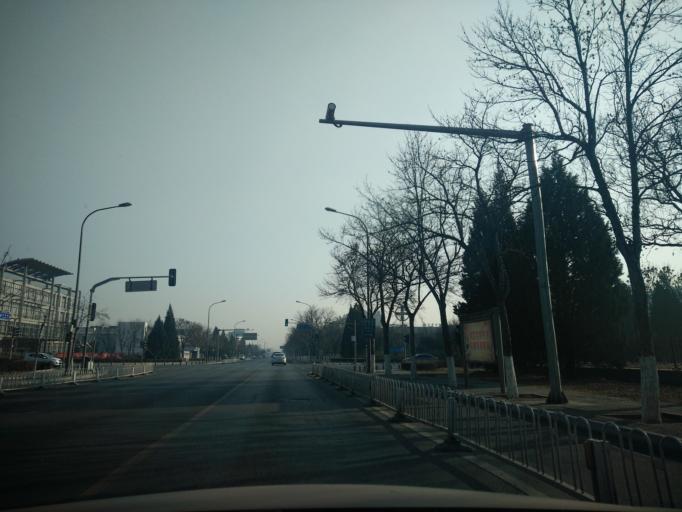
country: CN
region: Beijing
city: Jiugong
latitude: 39.7987
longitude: 116.5078
